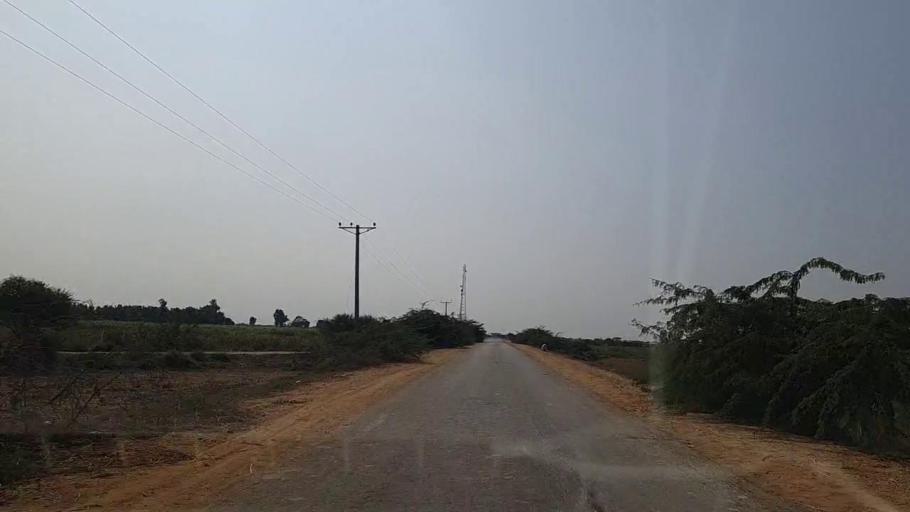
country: PK
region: Sindh
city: Chuhar Jamali
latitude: 24.2880
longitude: 67.9244
